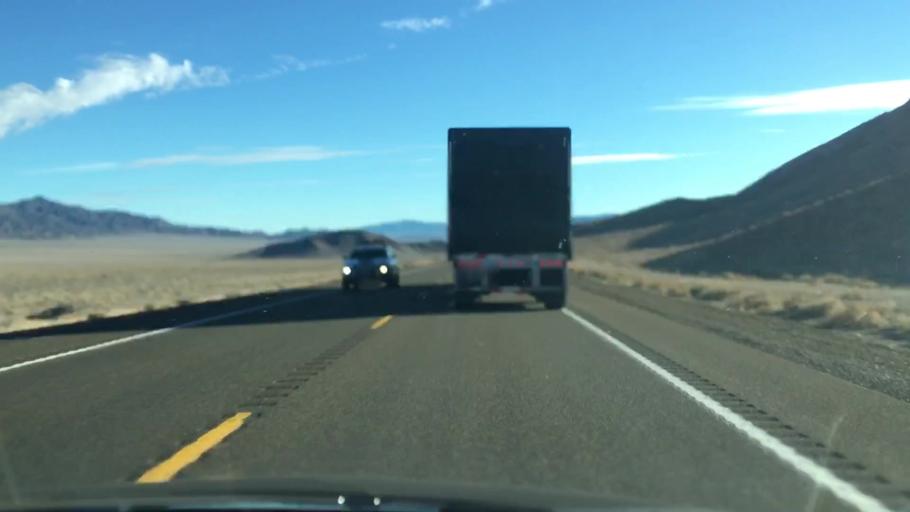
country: US
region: Nevada
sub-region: Nye County
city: Tonopah
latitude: 38.1675
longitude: -117.9550
